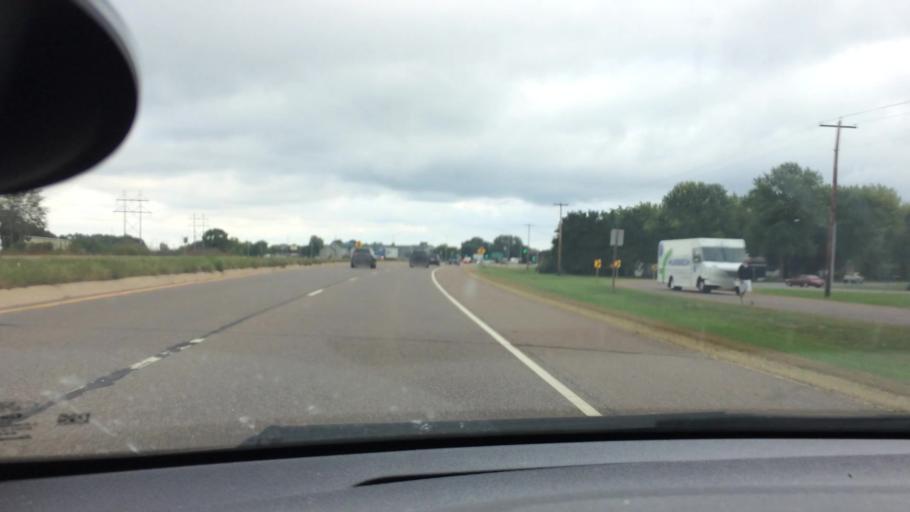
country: US
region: Wisconsin
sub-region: Chippewa County
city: Chippewa Falls
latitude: 44.9096
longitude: -91.4042
